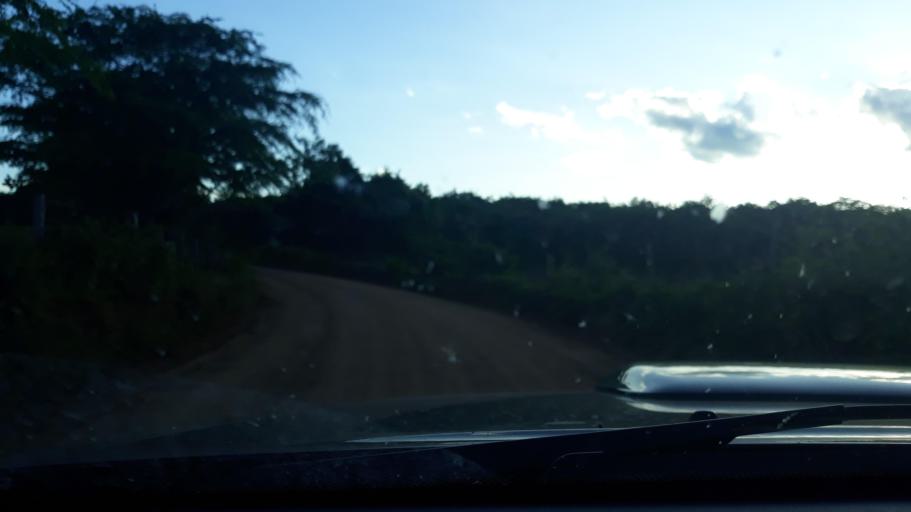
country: BR
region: Bahia
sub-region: Riacho De Santana
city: Riacho de Santana
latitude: -13.8141
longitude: -42.7223
